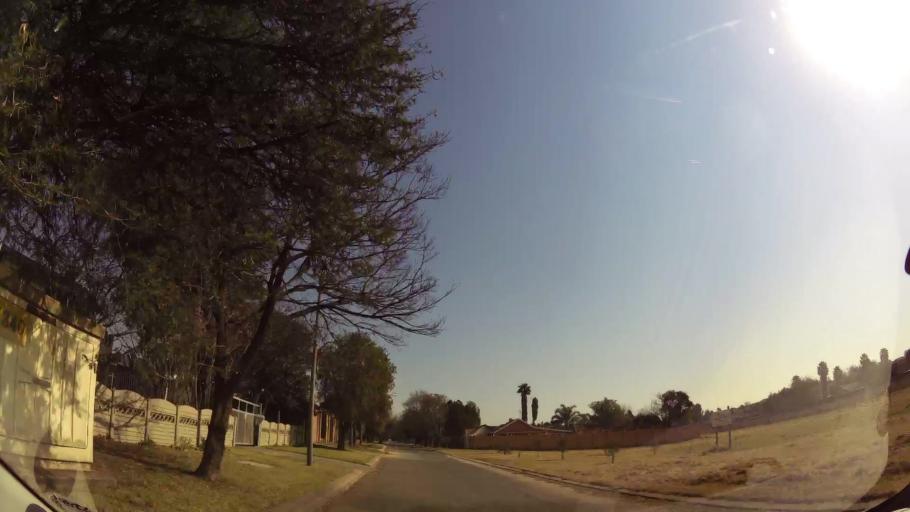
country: ZA
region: Gauteng
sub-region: Ekurhuleni Metropolitan Municipality
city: Boksburg
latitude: -26.1721
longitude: 28.2691
